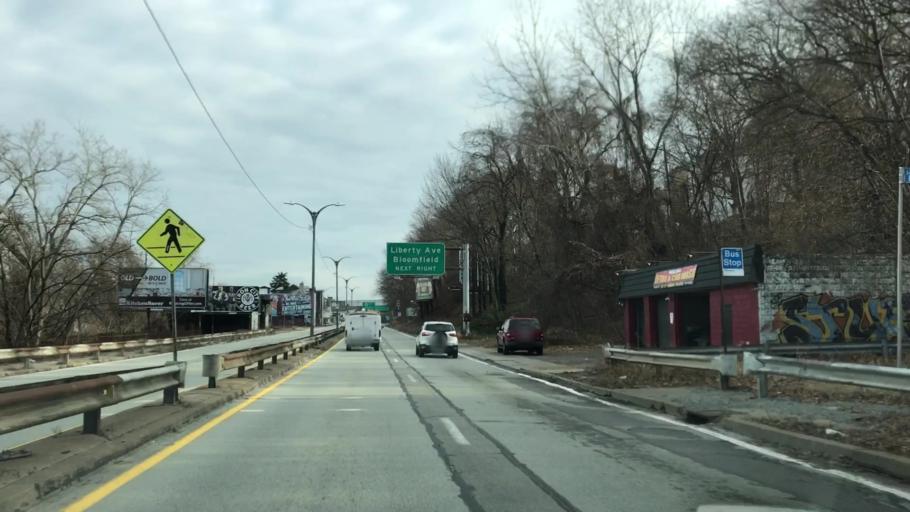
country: US
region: Pennsylvania
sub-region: Allegheny County
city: Bloomfield
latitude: 40.4566
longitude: -79.9636
